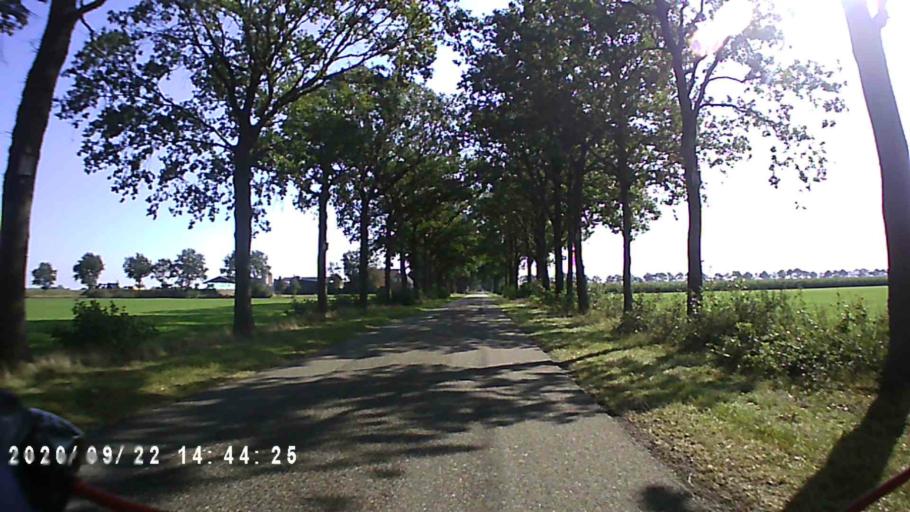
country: NL
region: Groningen
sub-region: Gemeente Leek
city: Leek
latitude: 53.0200
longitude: 6.3563
